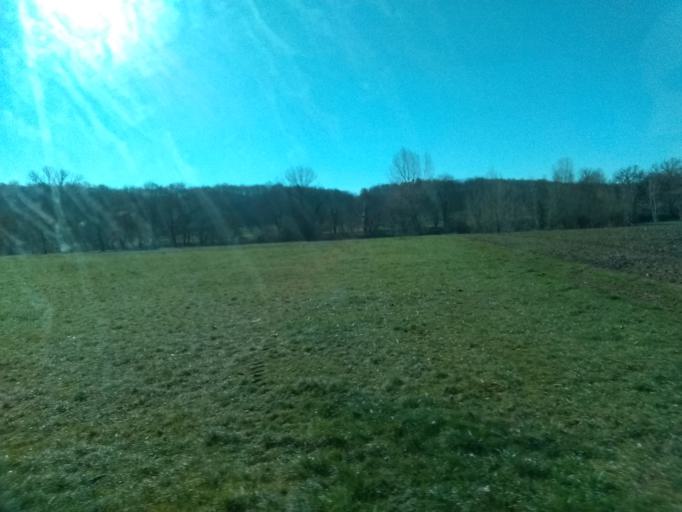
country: FR
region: Aquitaine
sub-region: Departement de la Dordogne
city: Montignac
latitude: 45.0957
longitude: 1.2029
